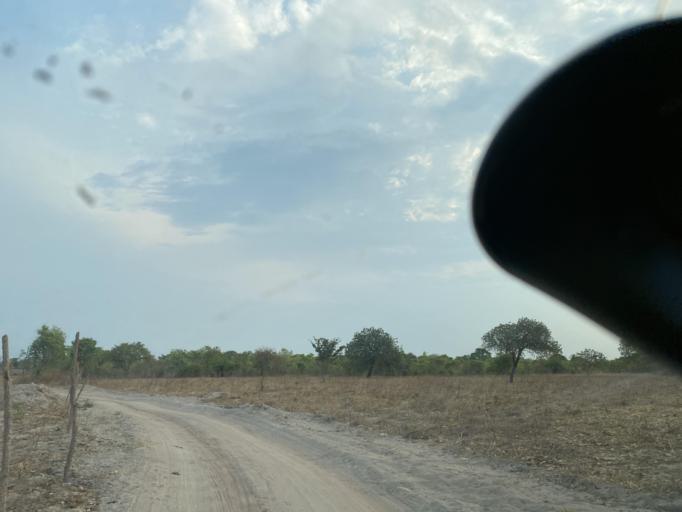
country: ZM
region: Lusaka
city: Chongwe
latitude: -15.2132
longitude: 28.5799
